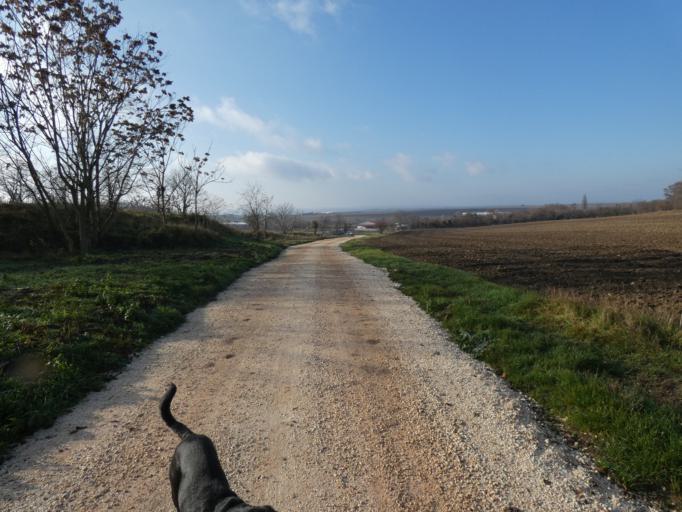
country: HU
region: Pest
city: Paty
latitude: 47.5024
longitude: 18.8312
